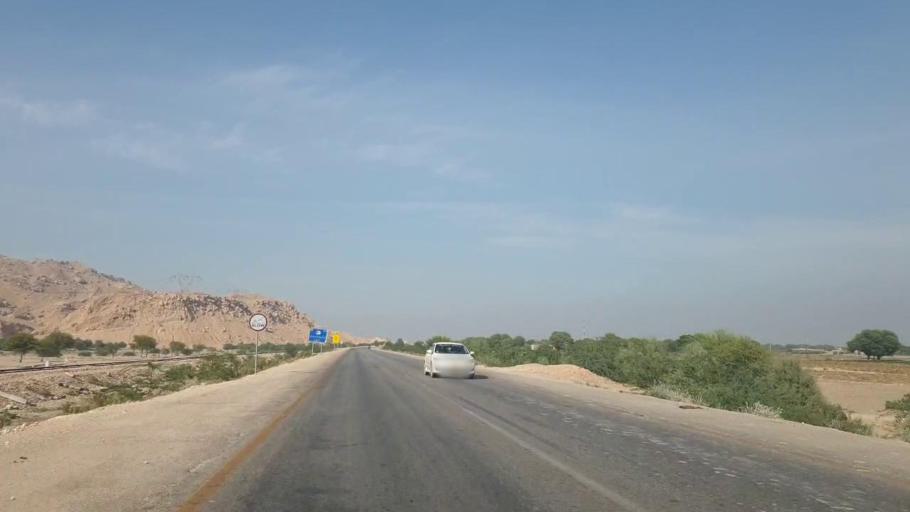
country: PK
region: Sindh
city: Sehwan
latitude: 26.2874
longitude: 67.8946
